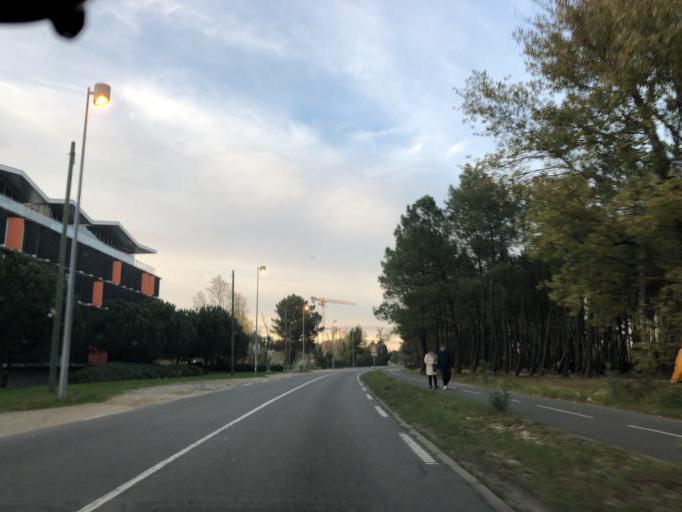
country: FR
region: Aquitaine
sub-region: Departement de la Gironde
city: Le Bouscat
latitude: 44.8801
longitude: -0.5834
